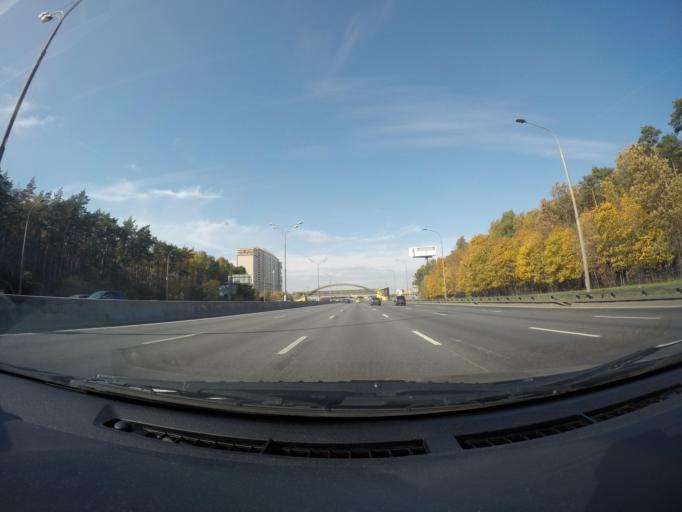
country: RU
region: Moscow
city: Babushkin
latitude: 55.8772
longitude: 37.7364
